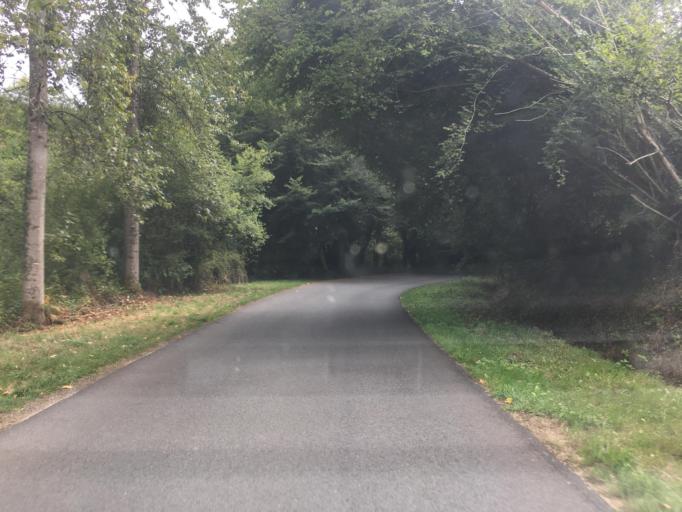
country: FR
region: Brittany
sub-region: Departement des Cotes-d'Armor
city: Gouarec
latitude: 48.2096
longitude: -3.1176
